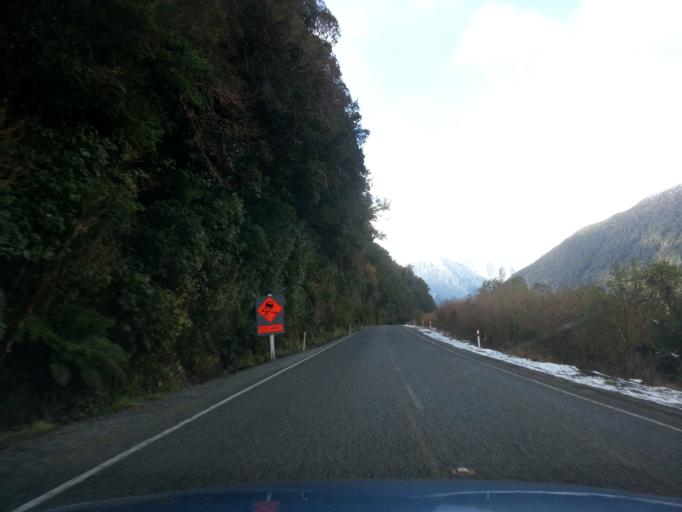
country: NZ
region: West Coast
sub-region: Grey District
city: Greymouth
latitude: -42.7840
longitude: 171.6067
